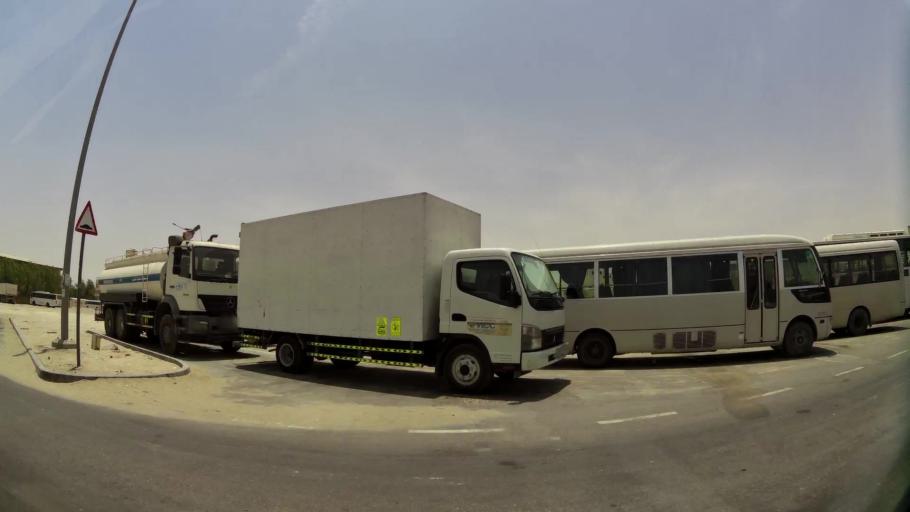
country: AE
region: Ash Shariqah
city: Sharjah
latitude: 25.2723
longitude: 55.4272
